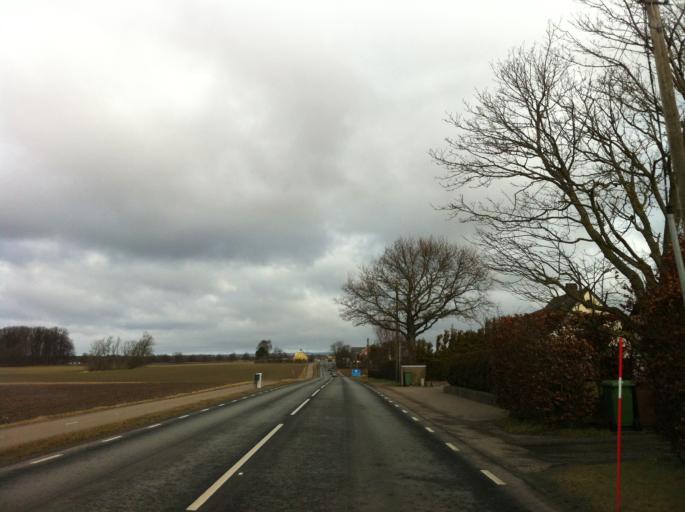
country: SE
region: Skane
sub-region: Angelholms Kommun
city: Strovelstorp
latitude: 56.1888
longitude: 12.8484
